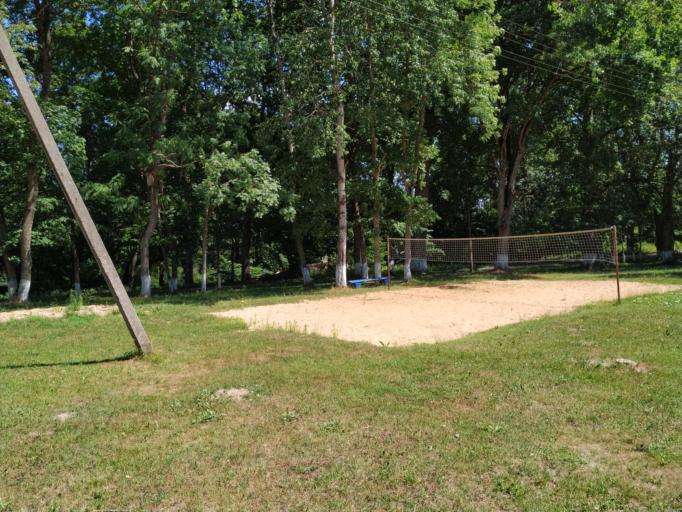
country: LT
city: Nemencine
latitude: 54.8992
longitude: 25.4792
